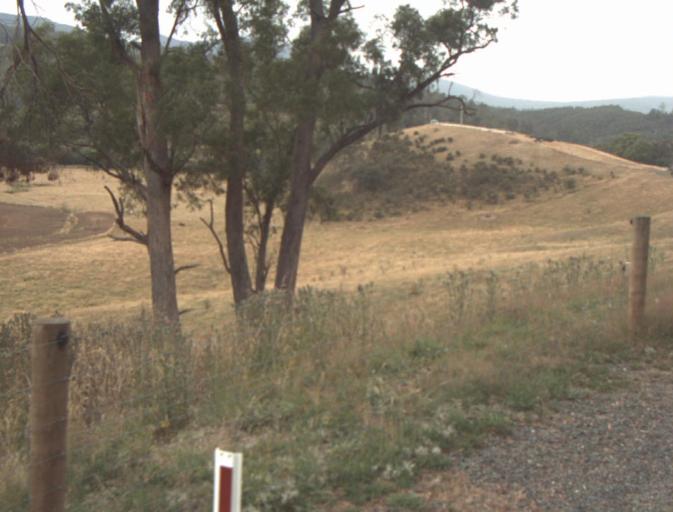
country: AU
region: Tasmania
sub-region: Northern Midlands
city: Evandale
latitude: -41.4695
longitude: 147.5349
